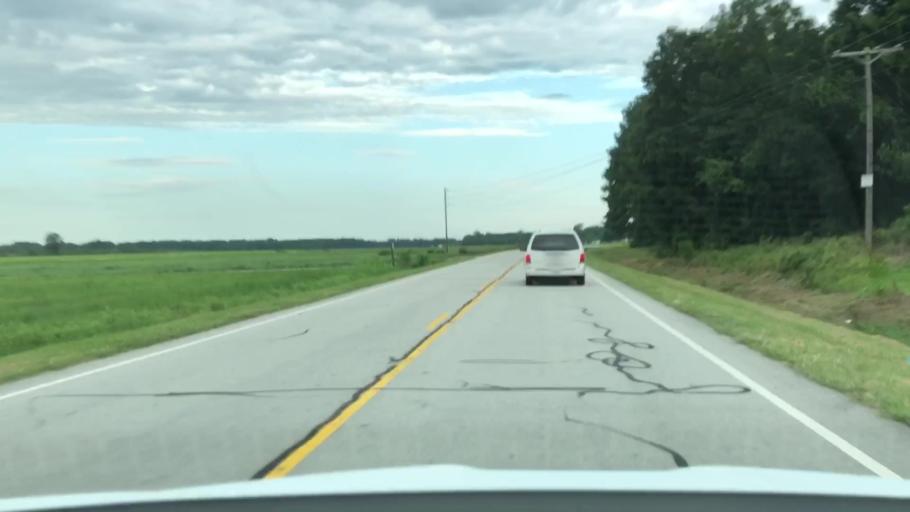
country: US
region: North Carolina
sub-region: Jones County
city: Trenton
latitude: 35.0791
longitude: -77.4283
